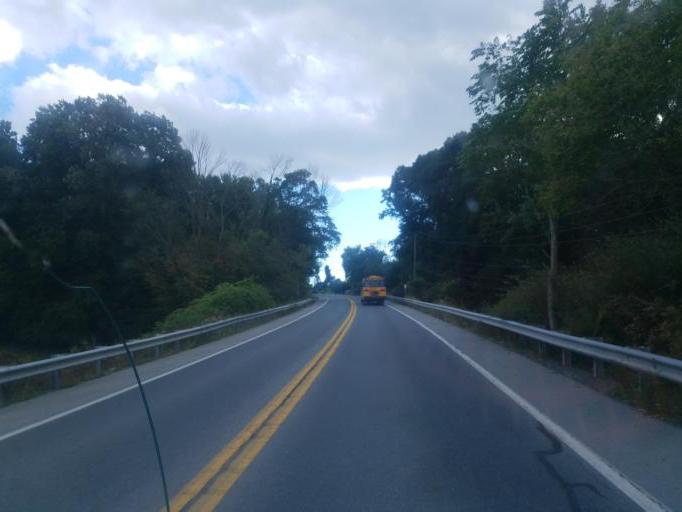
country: US
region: Pennsylvania
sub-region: Dauphin County
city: Middletown
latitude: 40.1464
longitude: -76.7178
